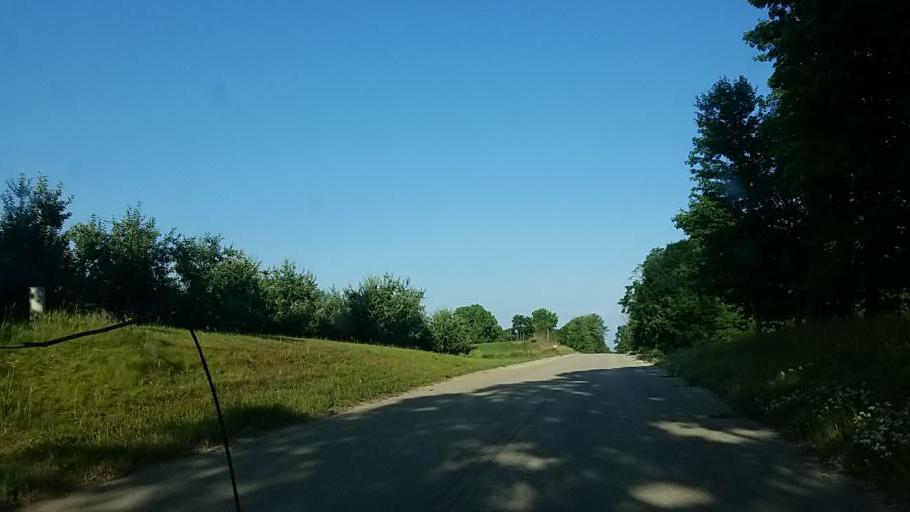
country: US
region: Michigan
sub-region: Newaygo County
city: Newaygo
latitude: 43.3656
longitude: -85.8443
